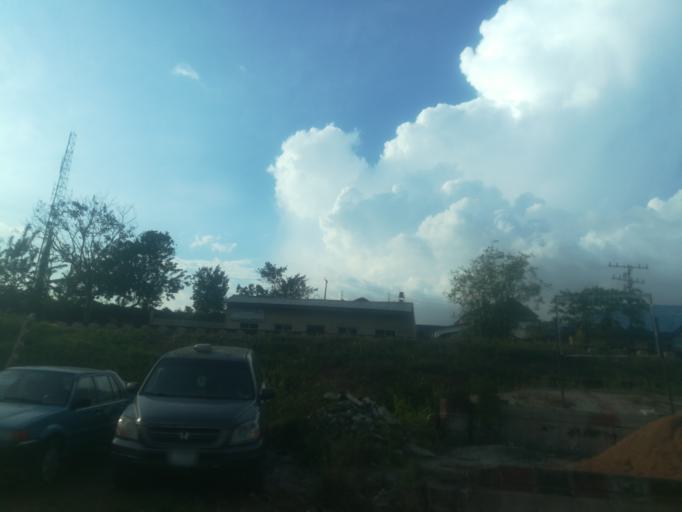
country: NG
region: Oyo
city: Ibadan
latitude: 7.3784
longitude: 3.8598
